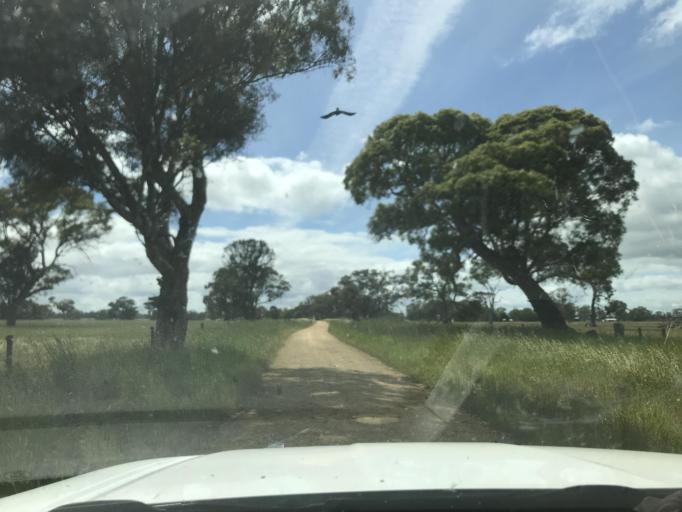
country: AU
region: South Australia
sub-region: Naracoorte and Lucindale
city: Naracoorte
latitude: -37.0185
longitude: 141.0928
